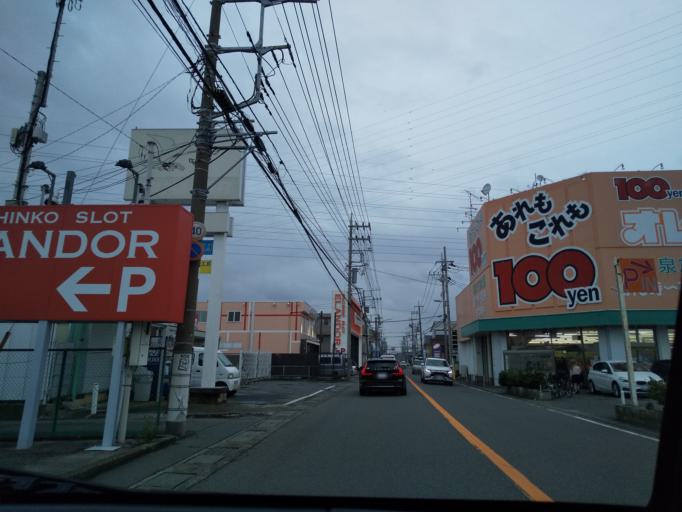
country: JP
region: Kanagawa
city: Fujisawa
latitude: 35.4029
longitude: 139.5015
